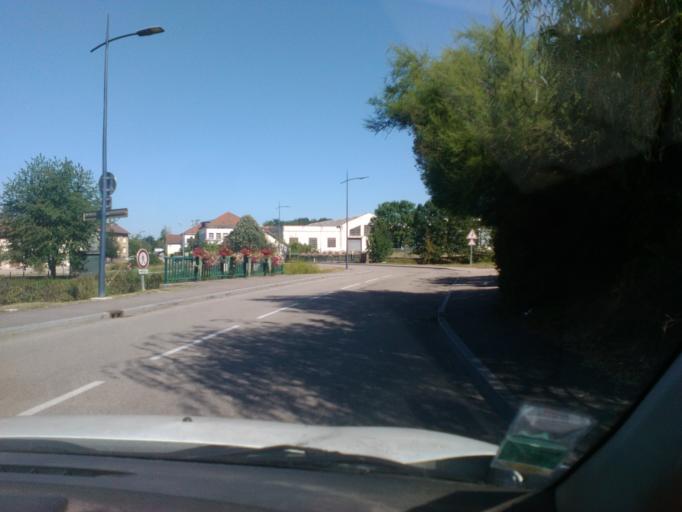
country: FR
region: Lorraine
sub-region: Departement des Vosges
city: Golbey
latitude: 48.2006
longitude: 6.4289
